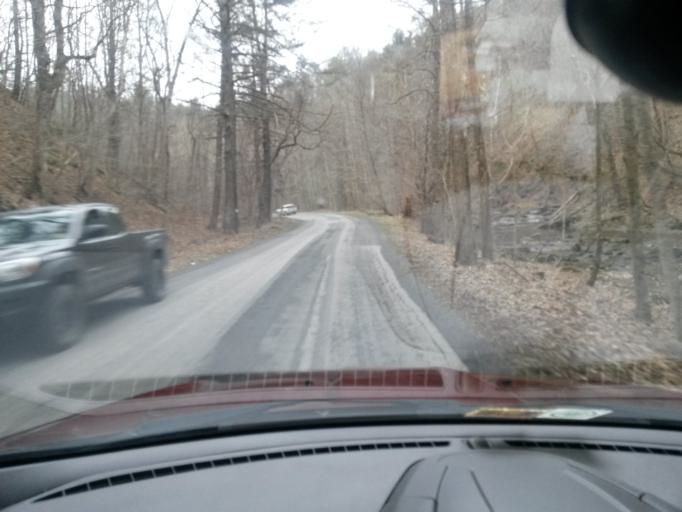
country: US
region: Virginia
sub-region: Bath County
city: Warm Springs
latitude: 38.0424
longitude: -79.8623
